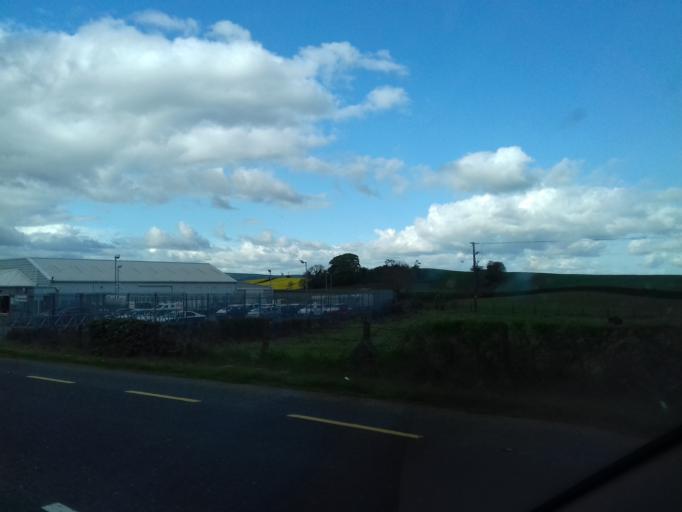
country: IE
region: Leinster
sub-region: Kilkenny
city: Kilkenny
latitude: 52.6273
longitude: -7.2511
